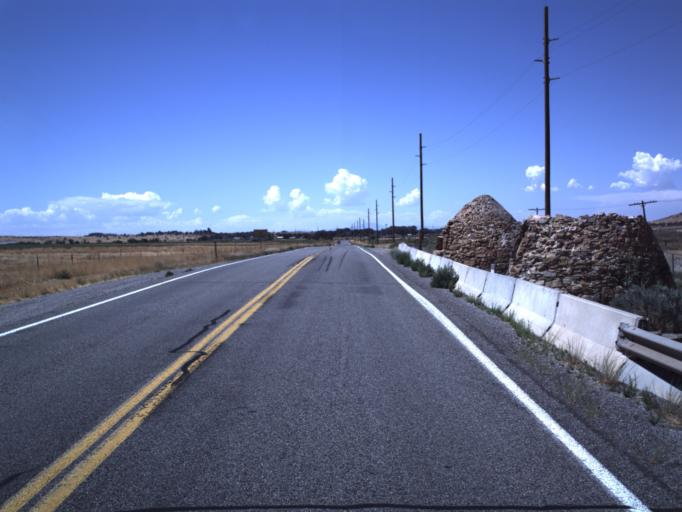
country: US
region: Utah
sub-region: Millard County
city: Delta
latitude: 39.5396
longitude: -112.2477
